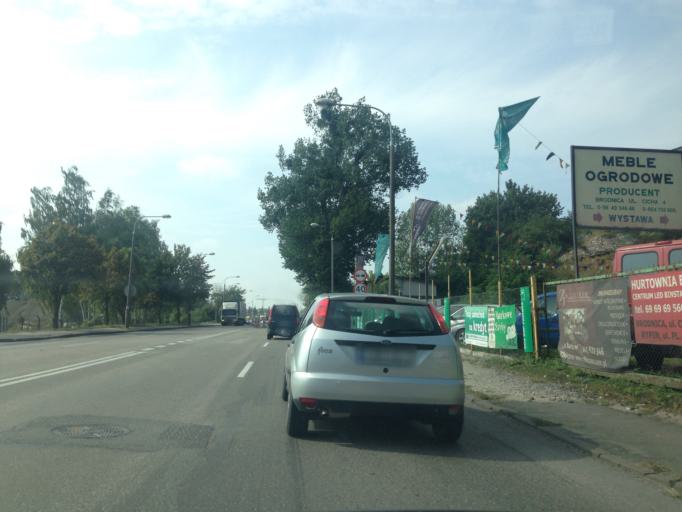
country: PL
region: Kujawsko-Pomorskie
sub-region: Powiat brodnicki
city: Brodnica
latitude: 53.2667
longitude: 19.4101
